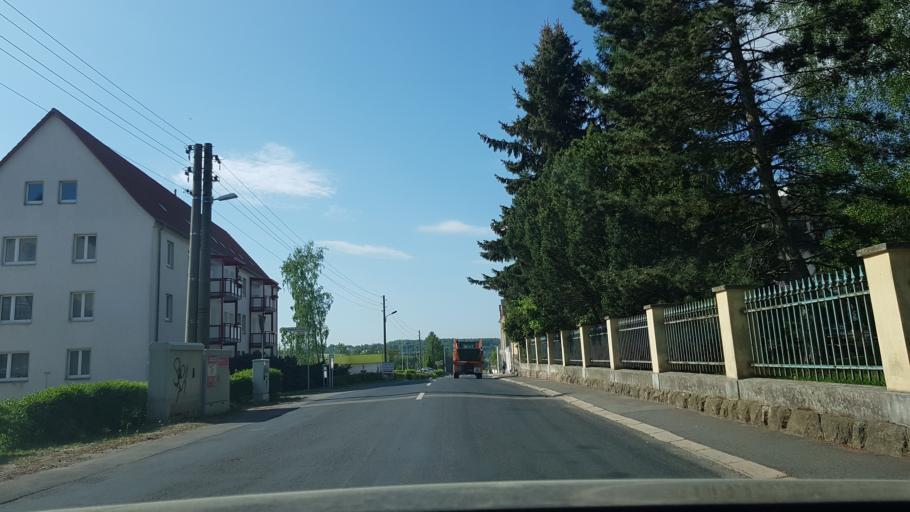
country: DE
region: Saxony
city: Wittgensdorf
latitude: 50.8767
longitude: 12.8711
